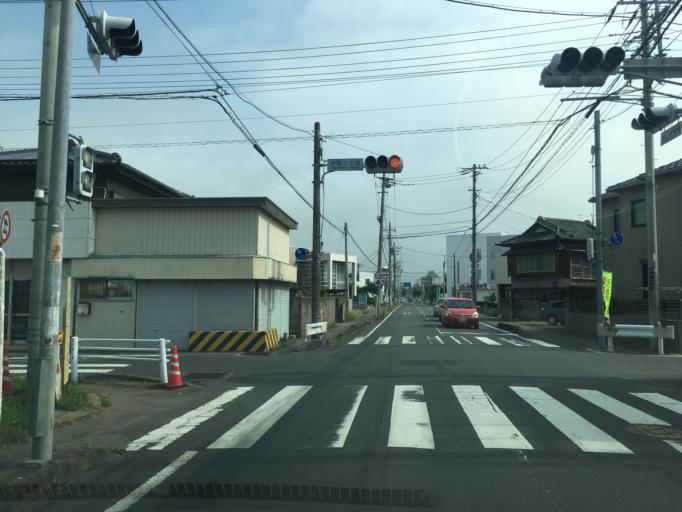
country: JP
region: Ibaraki
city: Oarai
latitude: 36.3440
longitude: 140.5827
